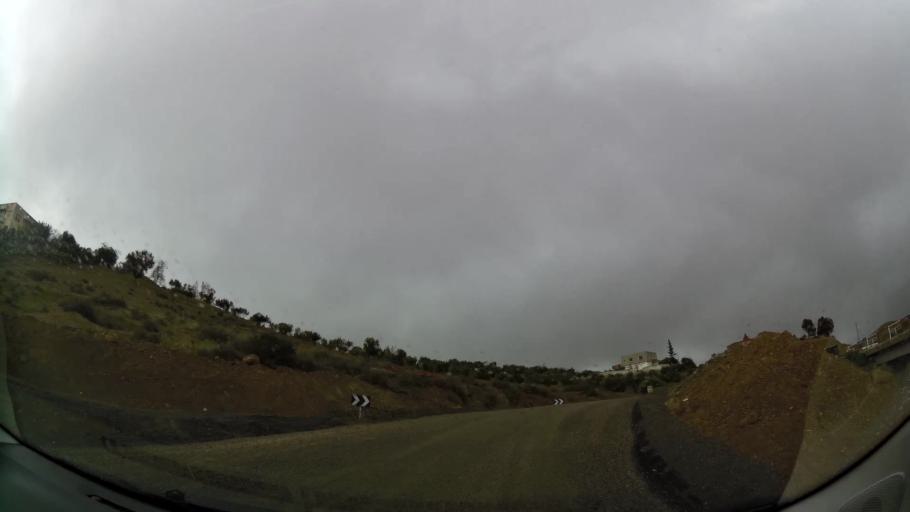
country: MA
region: Oriental
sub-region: Nador
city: Midar
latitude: 34.8910
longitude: -3.7596
